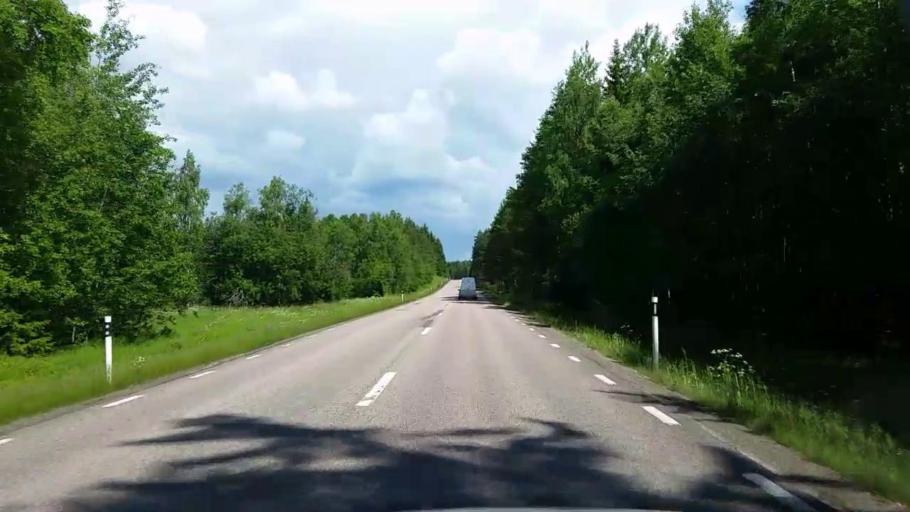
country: SE
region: Dalarna
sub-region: Avesta Kommun
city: Avesta
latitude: 60.1691
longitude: 16.2783
